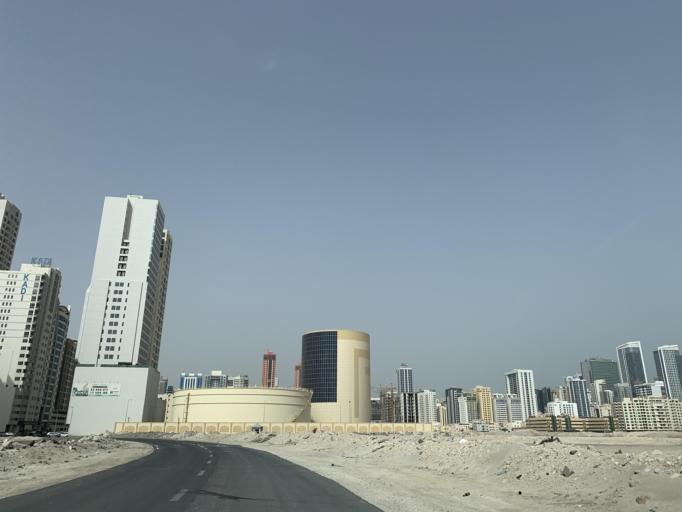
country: BH
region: Manama
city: Manama
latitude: 26.2160
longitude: 50.6212
